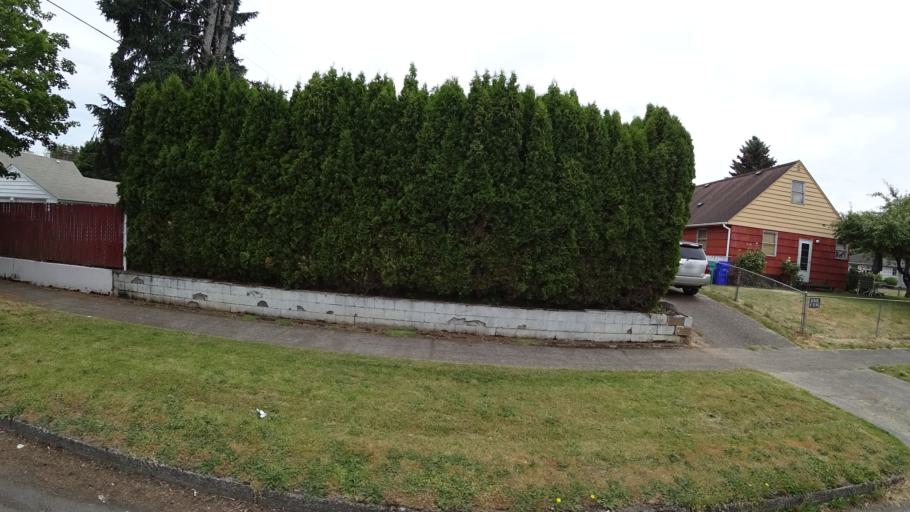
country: US
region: Oregon
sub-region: Multnomah County
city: Lents
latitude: 45.5112
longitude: -122.5721
